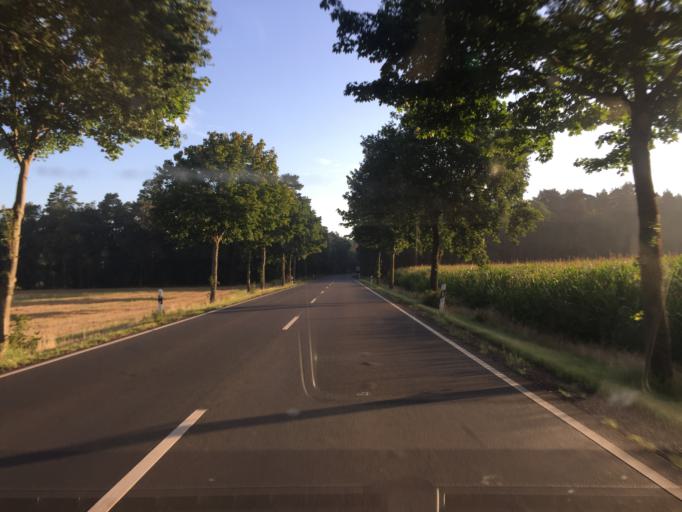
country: DE
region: Lower Saxony
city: Heemsen
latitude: 52.7312
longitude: 9.2933
